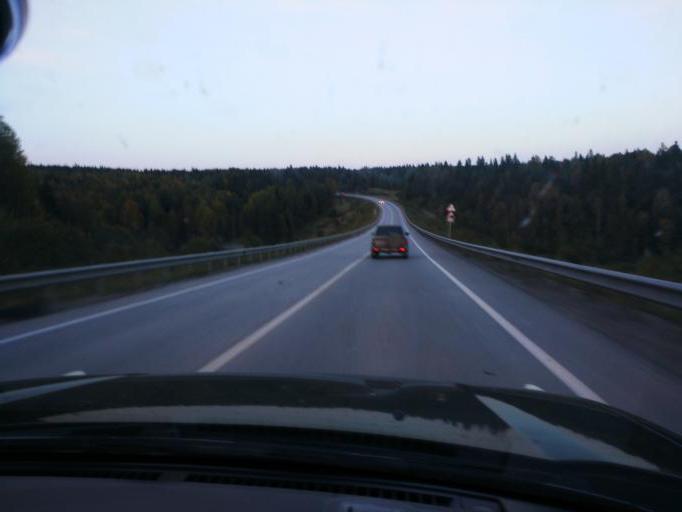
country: RU
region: Perm
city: Sylva
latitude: 58.2833
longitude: 56.7251
